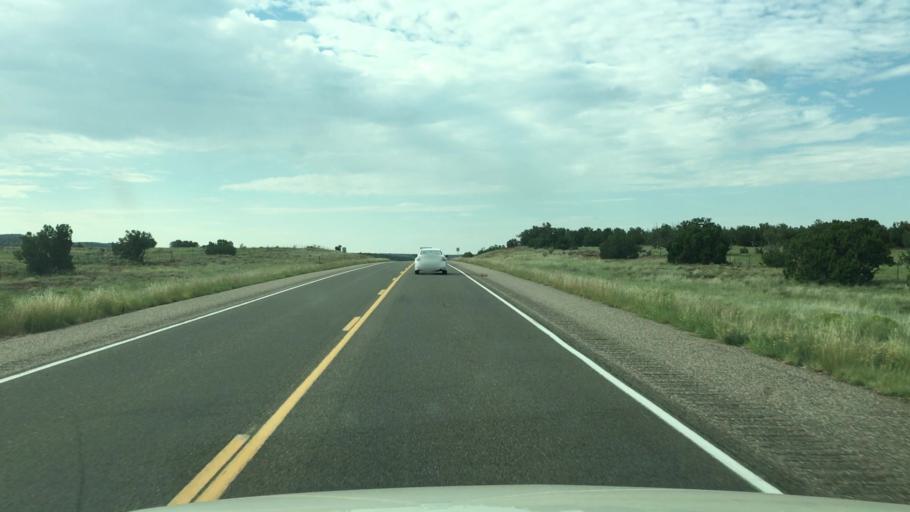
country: US
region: New Mexico
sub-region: Santa Fe County
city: Eldorado at Santa Fe
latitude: 35.3137
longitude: -105.8303
